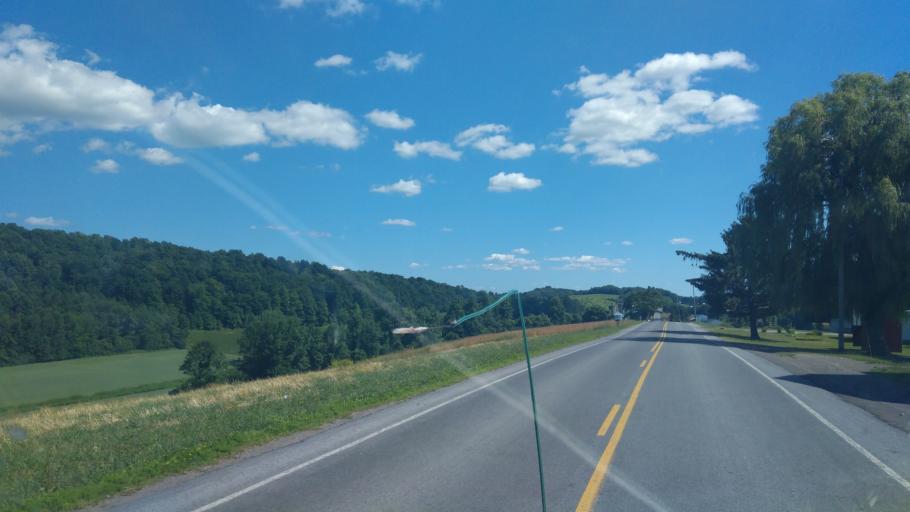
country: US
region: New York
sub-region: Wayne County
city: Lyons
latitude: 43.1233
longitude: -77.0128
